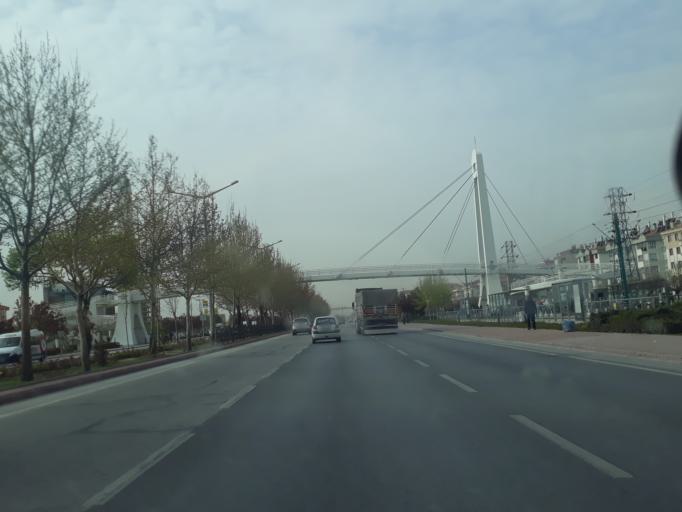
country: TR
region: Konya
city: Selcuklu
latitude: 37.9661
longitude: 32.5150
